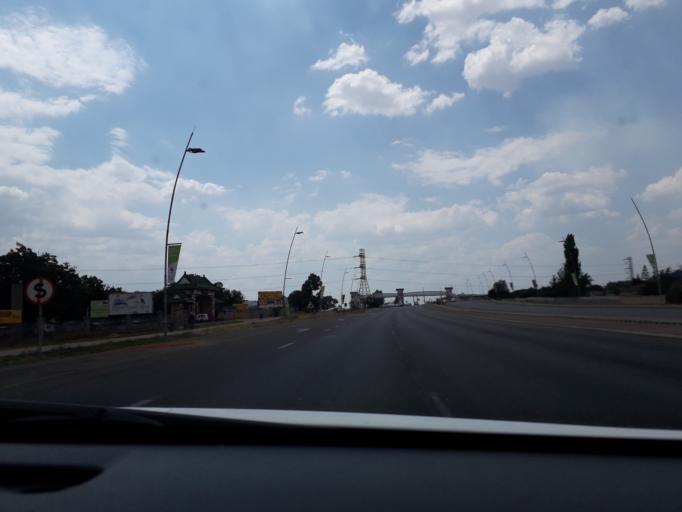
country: ZA
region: Gauteng
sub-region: City of Johannesburg Metropolitan Municipality
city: Modderfontein
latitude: -26.0828
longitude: 28.1896
